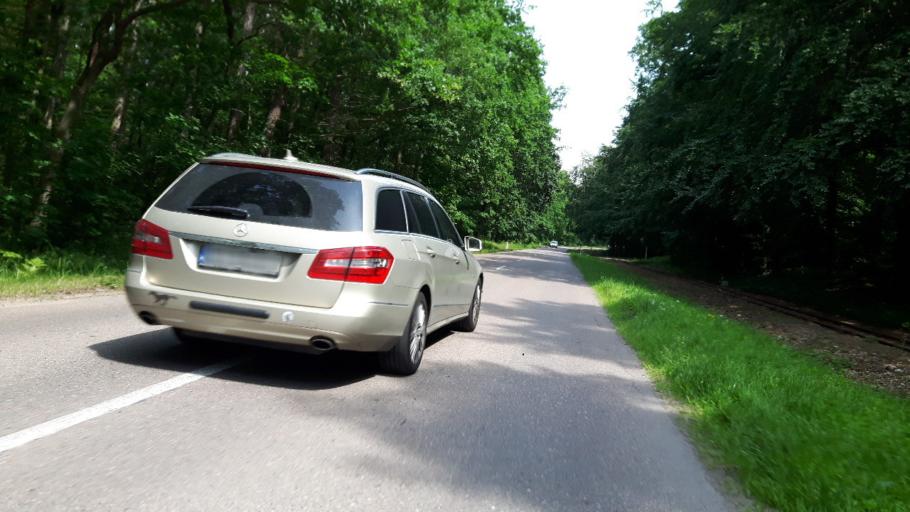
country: PL
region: Pomeranian Voivodeship
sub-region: Powiat nowodworski
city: Stegna
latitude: 54.3319
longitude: 19.0847
